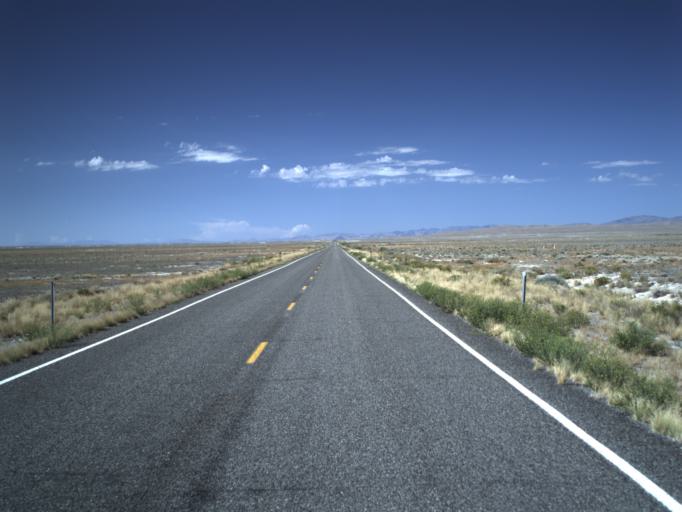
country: US
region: Utah
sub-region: Millard County
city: Delta
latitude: 39.2171
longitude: -112.9546
